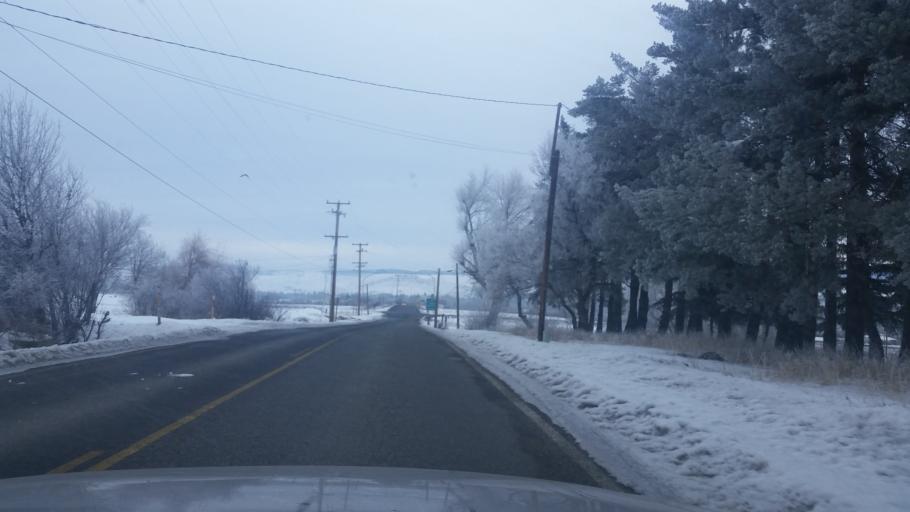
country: US
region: Washington
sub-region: Kittitas County
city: Ellensburg
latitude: 47.0515
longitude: -120.6662
